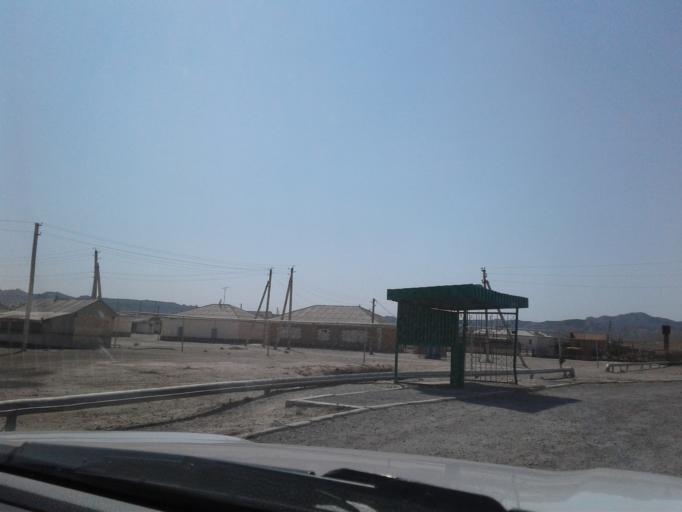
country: TM
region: Balkan
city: Gazanjyk
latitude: 39.1502
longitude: 55.3083
